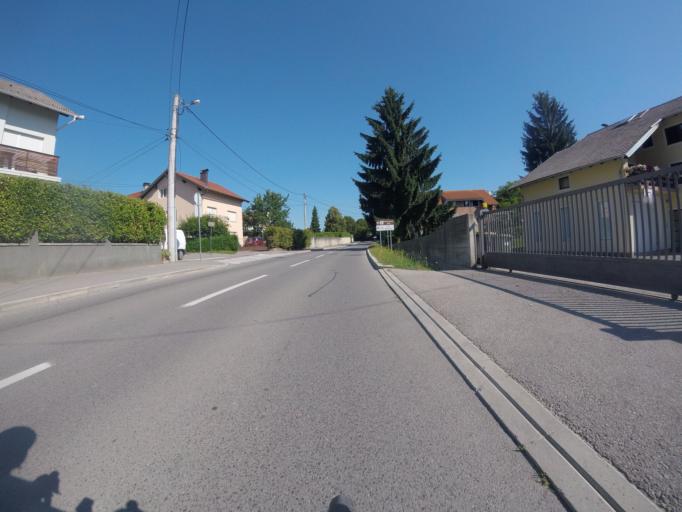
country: HR
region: Zagrebacka
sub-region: Grad Samobor
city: Samobor
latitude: 45.8150
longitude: 15.7051
